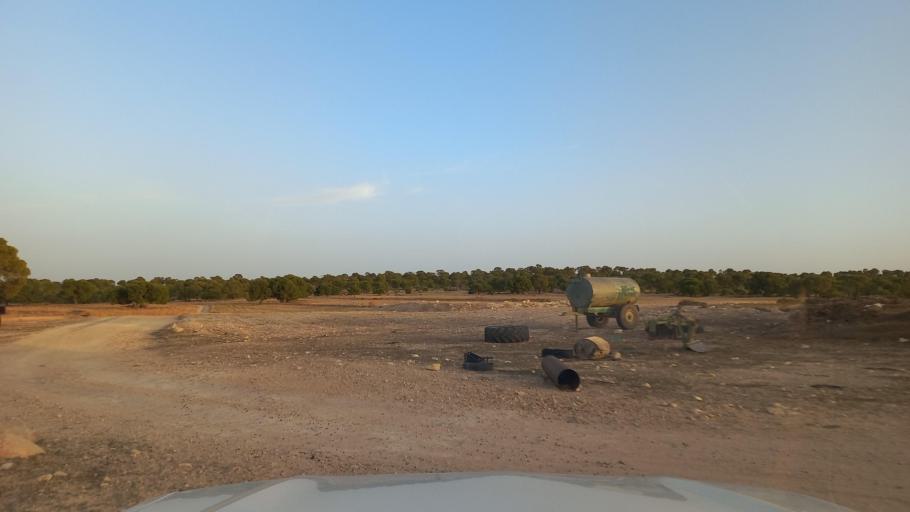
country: TN
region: Al Qasrayn
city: Sbiba
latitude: 35.4261
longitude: 8.9143
